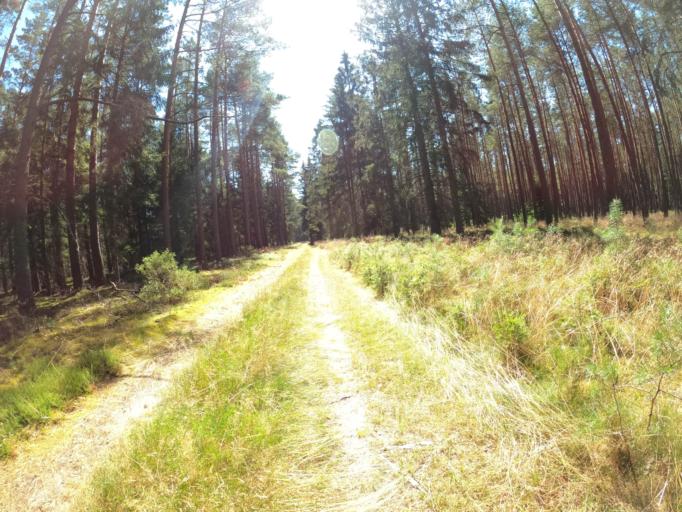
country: PL
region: West Pomeranian Voivodeship
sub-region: Powiat bialogardzki
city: Tychowo
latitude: 54.0612
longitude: 16.3672
